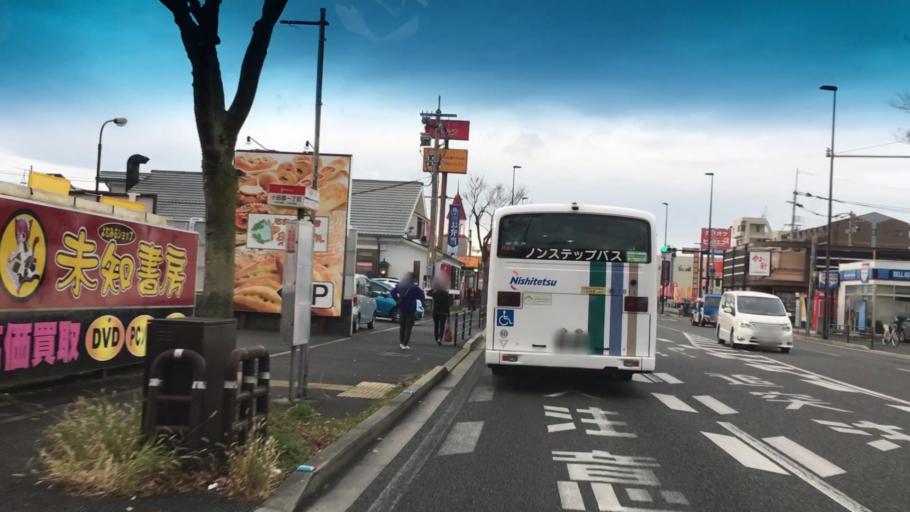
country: JP
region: Fukuoka
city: Fukuoka-shi
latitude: 33.5677
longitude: 130.3368
